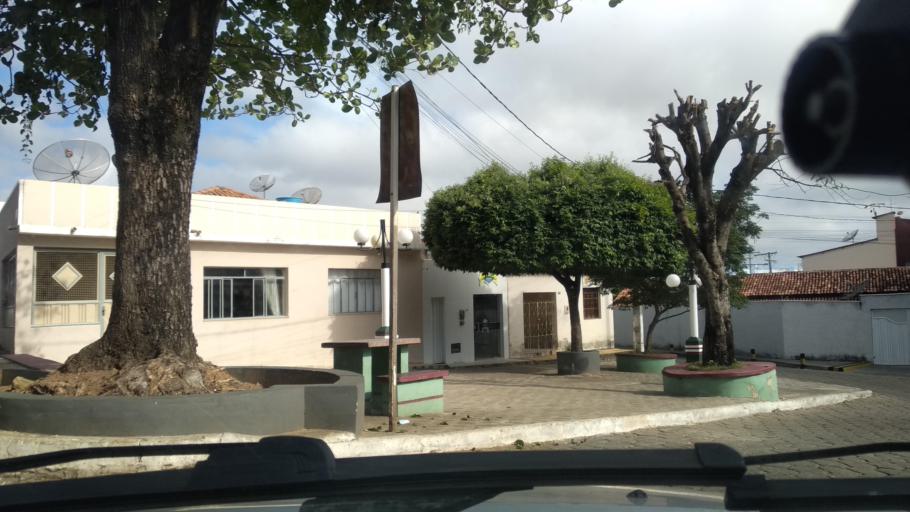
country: BR
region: Bahia
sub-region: Caetite
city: Caetite
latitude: -14.0706
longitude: -42.4918
